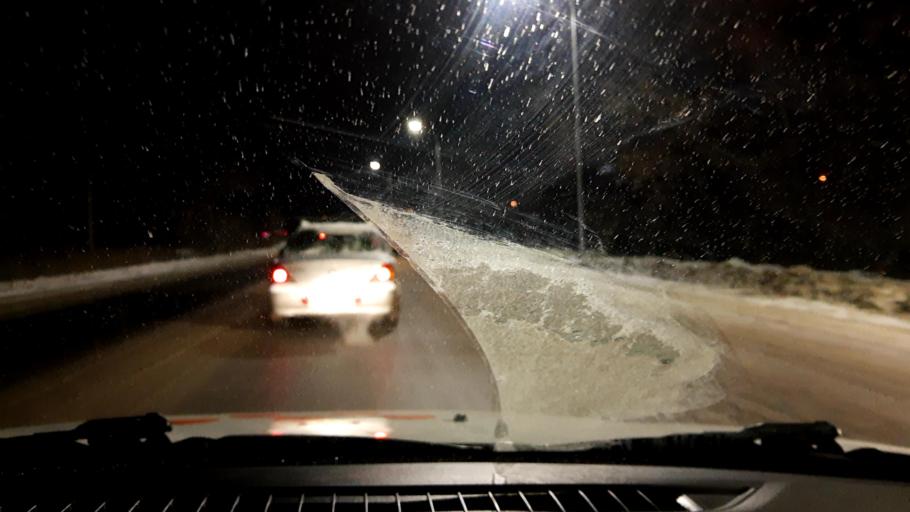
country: RU
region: Nizjnij Novgorod
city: Dzerzhinsk
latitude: 56.2415
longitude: 43.5166
